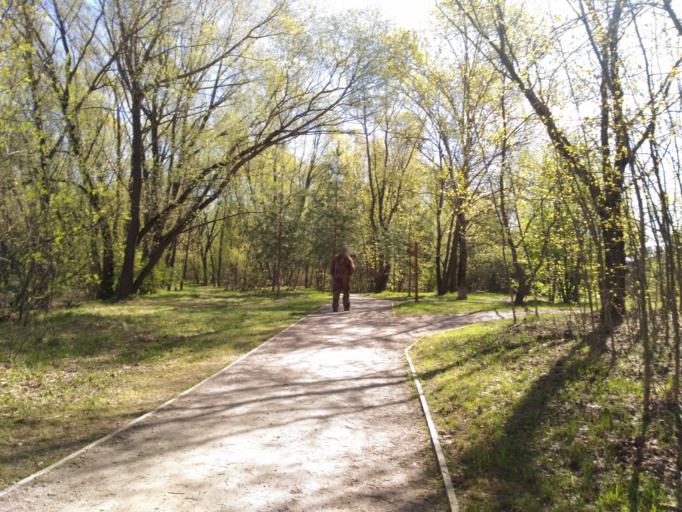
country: RU
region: Moscow
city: Shchukino
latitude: 55.7769
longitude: 37.4303
